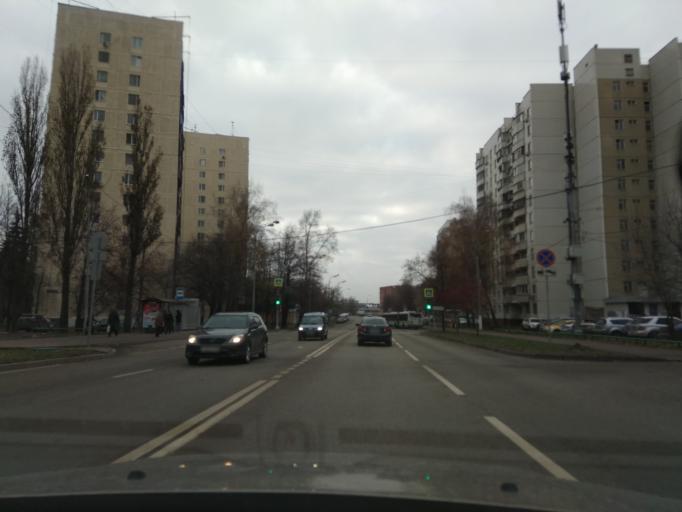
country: RU
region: Moscow
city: Likhobory
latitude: 55.8575
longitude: 37.5673
